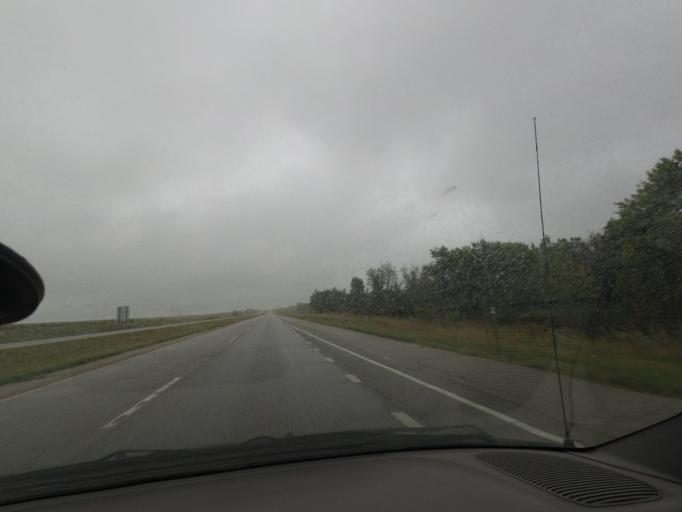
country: US
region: Illinois
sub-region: Pike County
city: Barry
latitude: 39.7027
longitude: -91.0333
